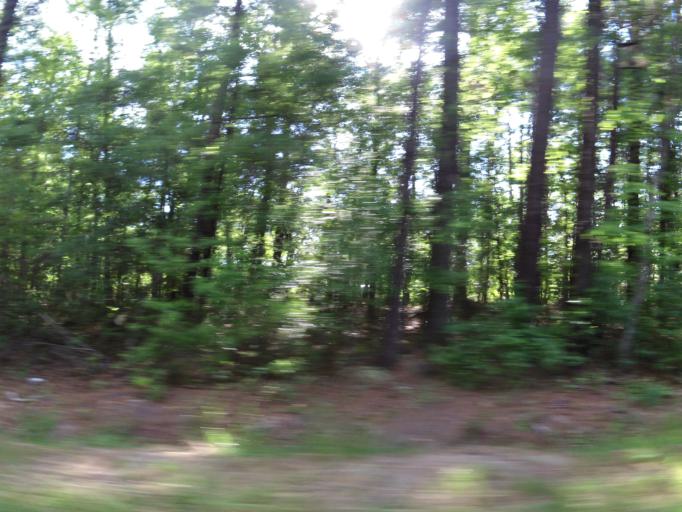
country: US
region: South Carolina
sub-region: Allendale County
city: Fairfax
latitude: 32.8688
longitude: -81.2382
